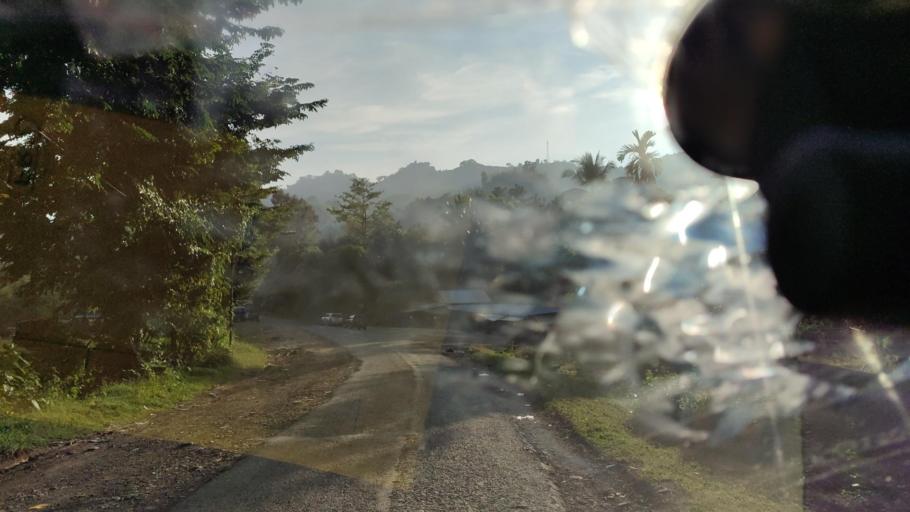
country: MM
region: Magway
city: Minbu
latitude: 19.8624
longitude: 94.1408
